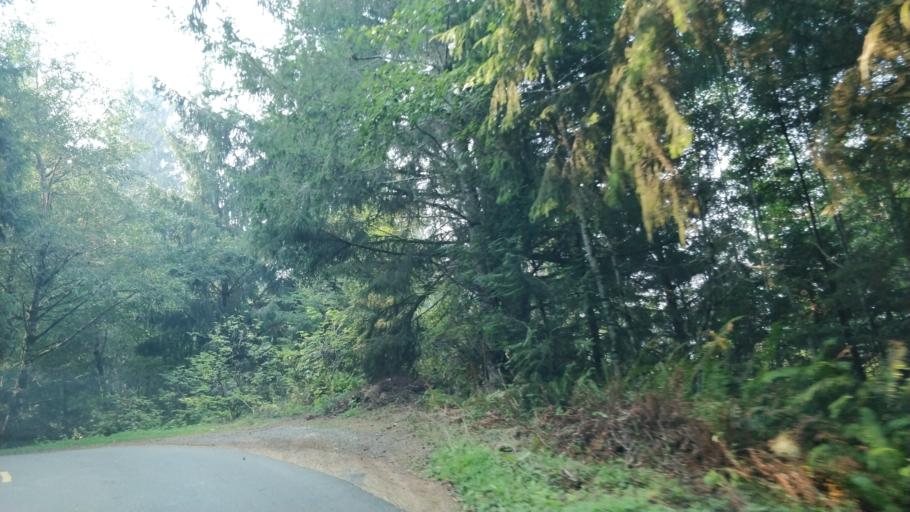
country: US
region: California
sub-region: Humboldt County
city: Ferndale
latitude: 40.5440
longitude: -124.2747
